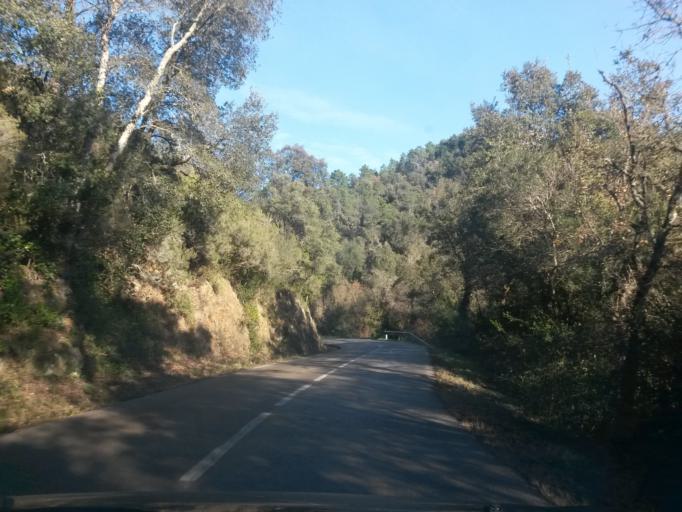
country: ES
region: Catalonia
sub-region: Provincia de Girona
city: Sant Gregori
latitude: 41.9864
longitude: 2.6852
